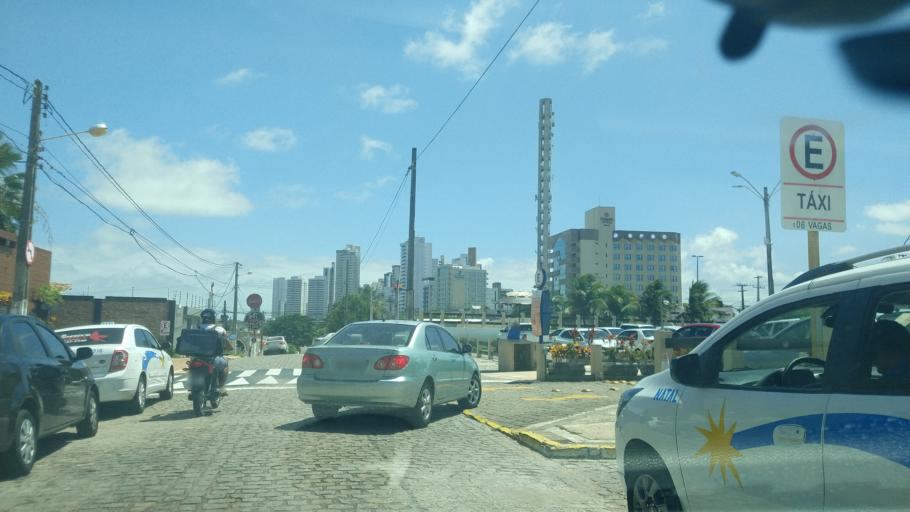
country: BR
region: Rio Grande do Norte
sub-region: Natal
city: Natal
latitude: -5.8691
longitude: -35.1814
